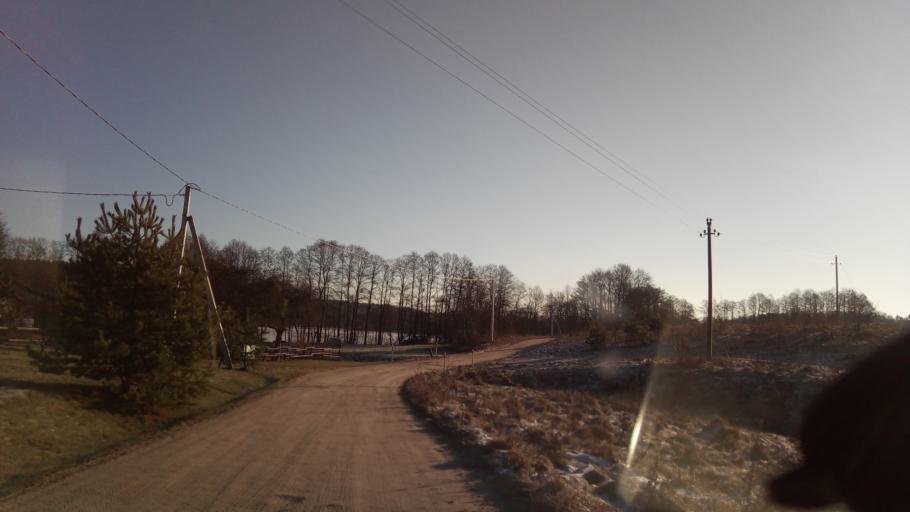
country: LT
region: Alytaus apskritis
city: Druskininkai
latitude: 54.1045
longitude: 24.0139
